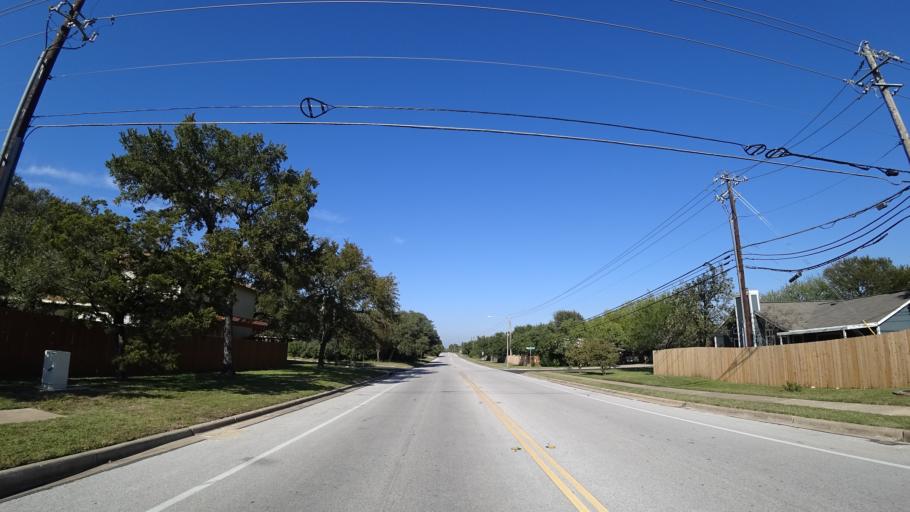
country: US
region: Texas
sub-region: Travis County
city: Shady Hollow
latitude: 30.2068
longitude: -97.8559
